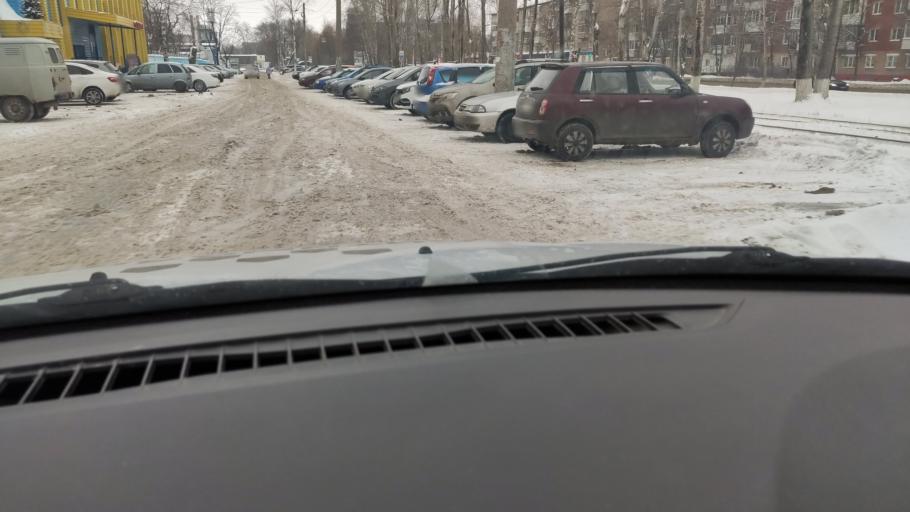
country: RU
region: Perm
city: Froly
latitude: 57.9583
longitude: 56.2436
